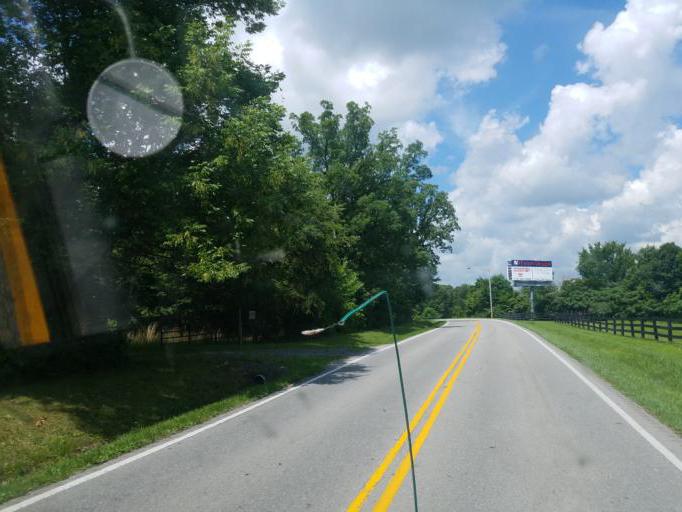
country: US
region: Kentucky
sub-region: Grayson County
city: Leitchfield
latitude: 37.4910
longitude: -86.2464
